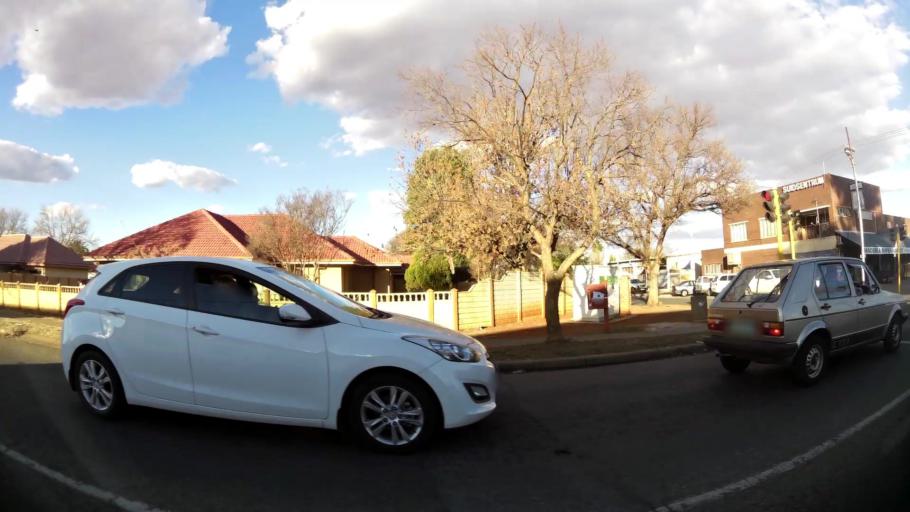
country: ZA
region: North-West
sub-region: Dr Kenneth Kaunda District Municipality
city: Potchefstroom
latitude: -26.7243
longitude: 27.0962
